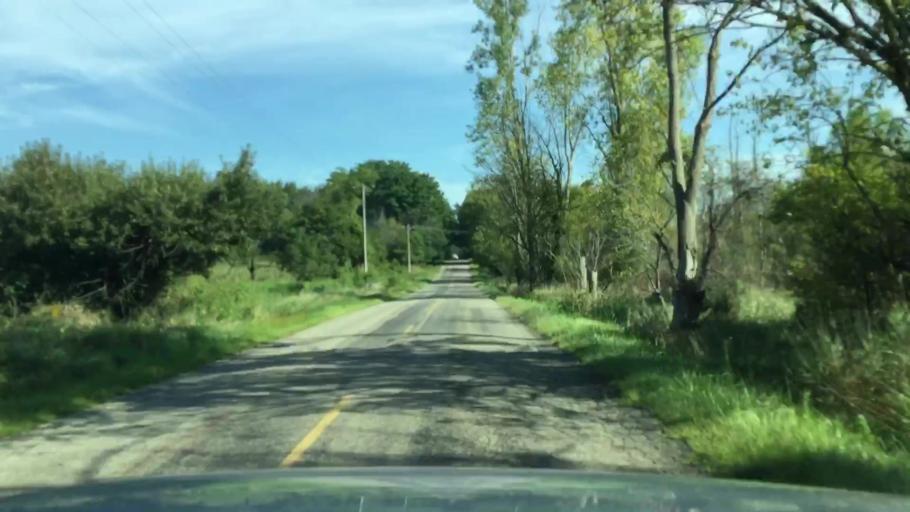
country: US
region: Michigan
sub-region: Lenawee County
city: Hudson
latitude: 41.9067
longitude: -84.4204
